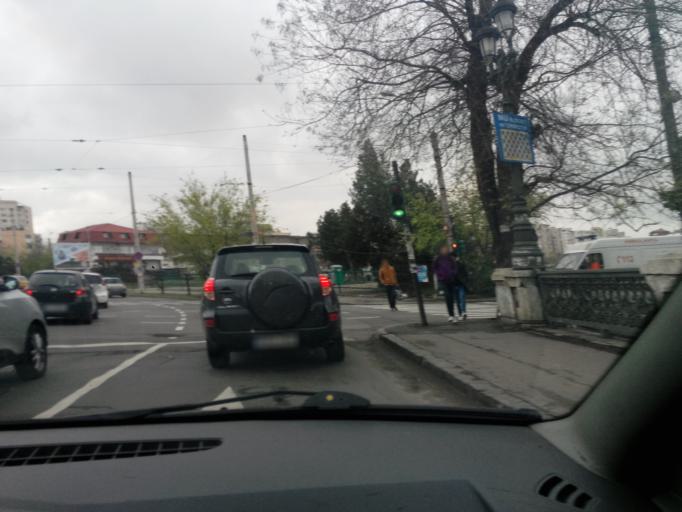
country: RO
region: Bucuresti
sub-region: Municipiul Bucuresti
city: Bucharest
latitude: 44.4170
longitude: 26.1138
